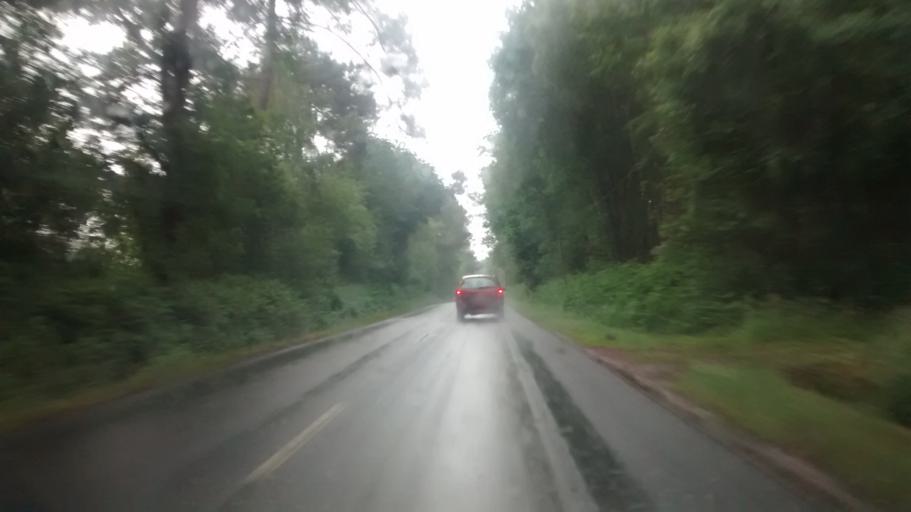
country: FR
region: Brittany
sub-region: Departement du Morbihan
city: La Gacilly
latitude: 47.7823
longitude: -2.1920
